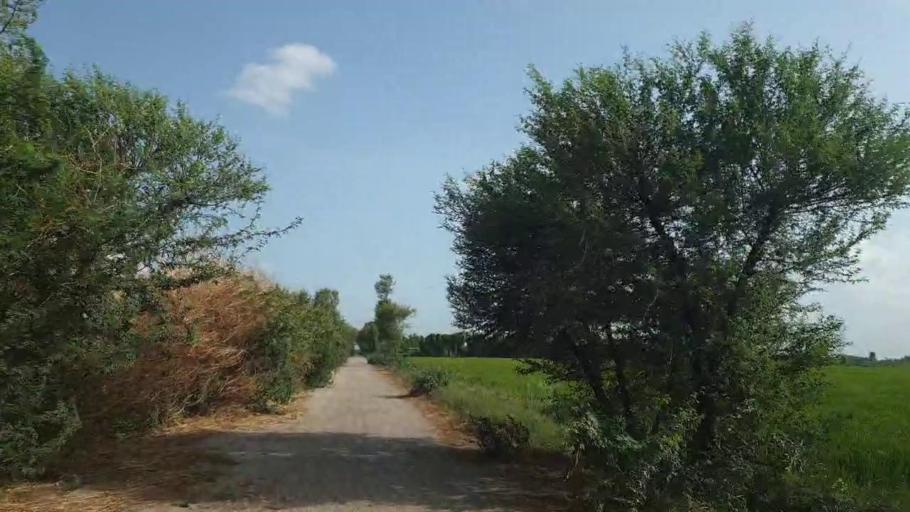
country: PK
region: Sindh
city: Kadhan
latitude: 24.6251
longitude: 69.0959
